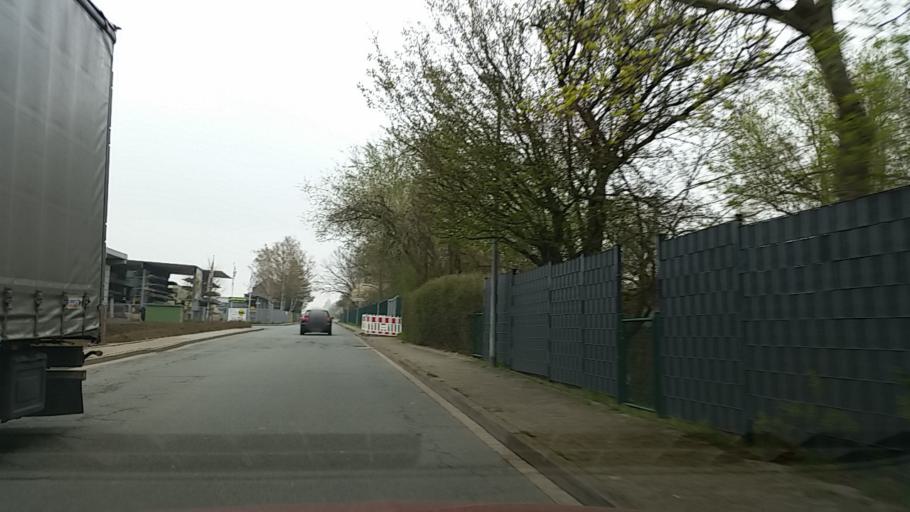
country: DE
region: Lower Saxony
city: Weyhausen
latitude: 52.3944
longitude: 10.7129
